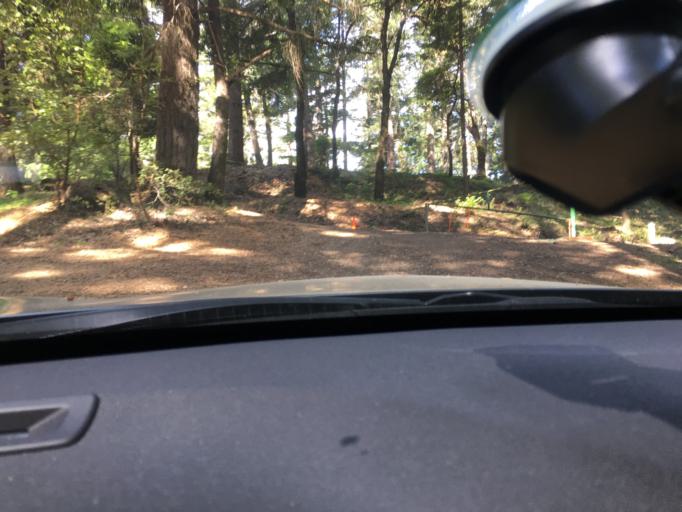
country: US
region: California
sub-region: Santa Clara County
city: Loyola
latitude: 37.2493
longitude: -122.1460
